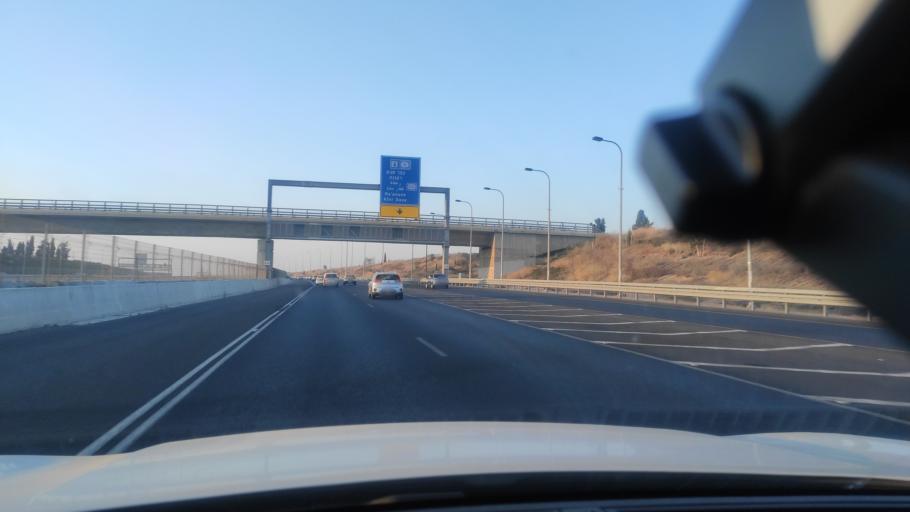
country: IL
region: Tel Aviv
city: Kefar Shemaryahu
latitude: 32.1823
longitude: 34.8272
